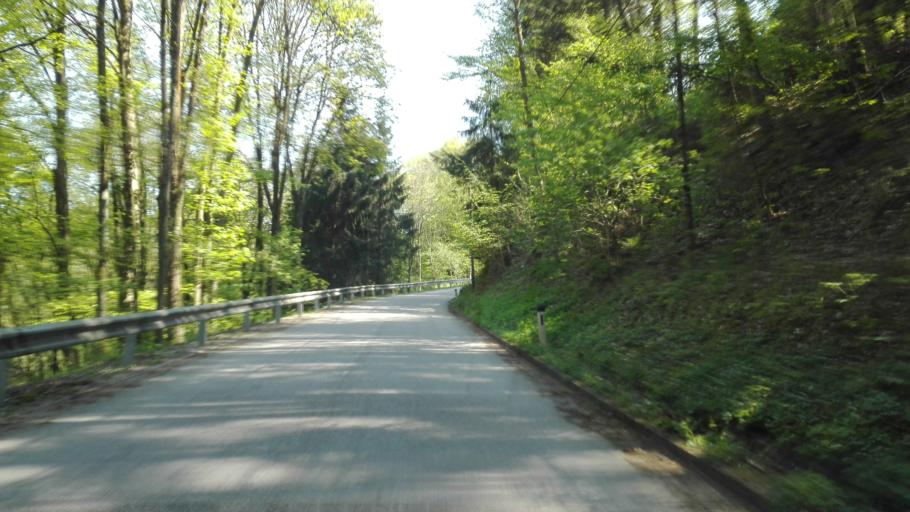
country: AT
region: Upper Austria
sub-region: Politischer Bezirk Rohrbach
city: Atzesberg
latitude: 48.4367
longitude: 13.9174
